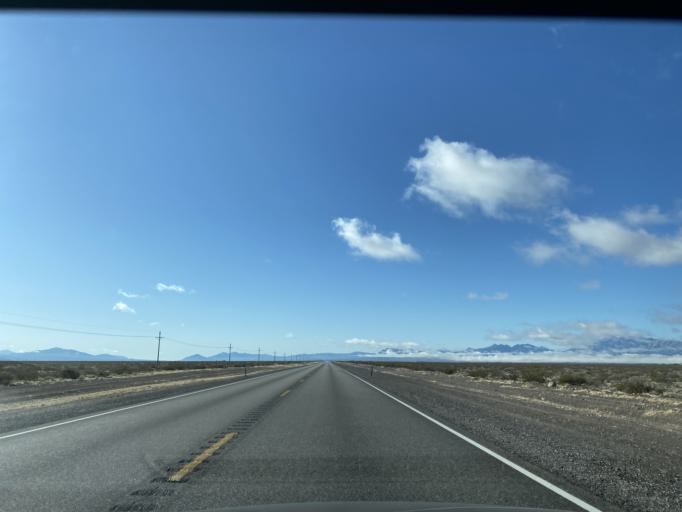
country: US
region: Nevada
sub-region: Nye County
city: Beatty
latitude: 36.6169
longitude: -116.4051
